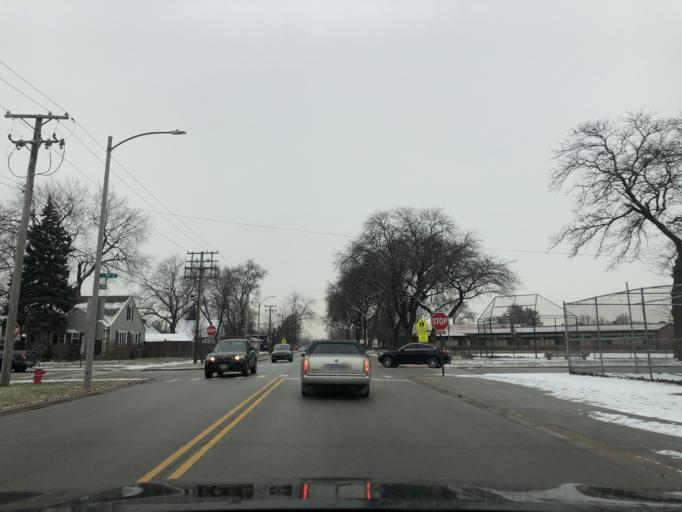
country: US
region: Illinois
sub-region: Cook County
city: Evergreen Park
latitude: 41.7303
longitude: -87.6922
